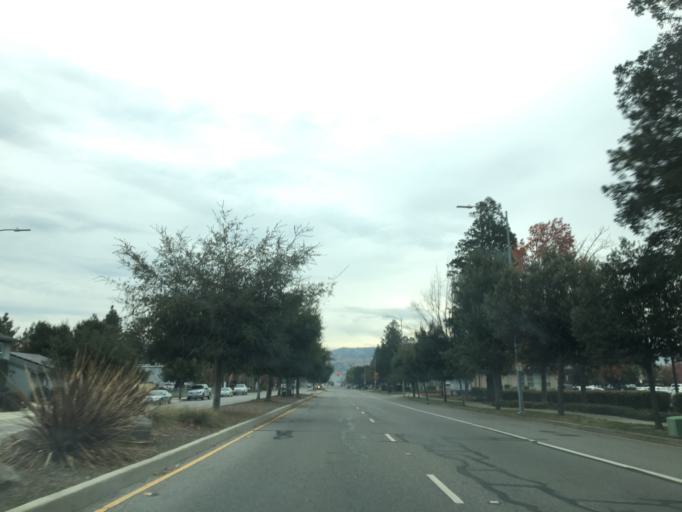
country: US
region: California
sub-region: Santa Clara County
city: Morgan Hill
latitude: 37.1139
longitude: -121.6404
